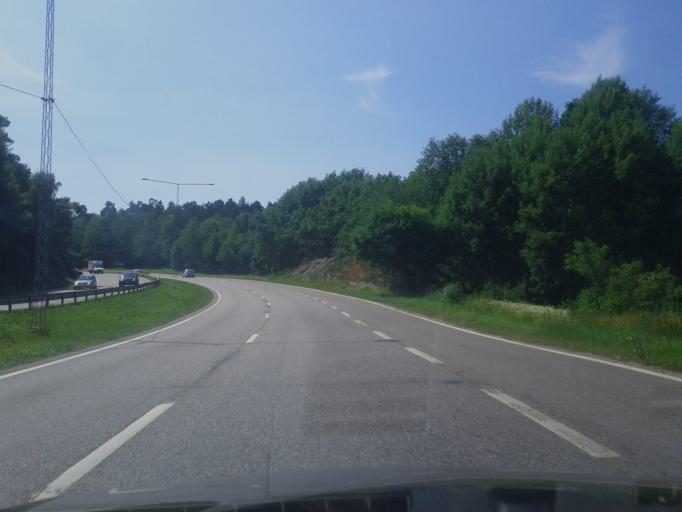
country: SE
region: Stockholm
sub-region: Huddinge Kommun
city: Huddinge
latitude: 59.2679
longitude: 18.0061
